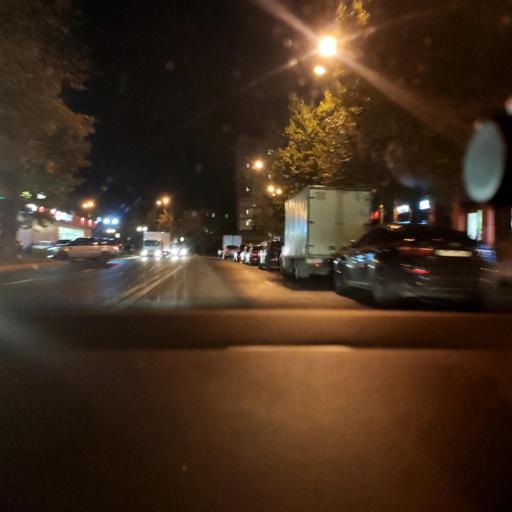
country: RU
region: Moskovskaya
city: Kotel'niki
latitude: 55.6378
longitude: 37.8415
